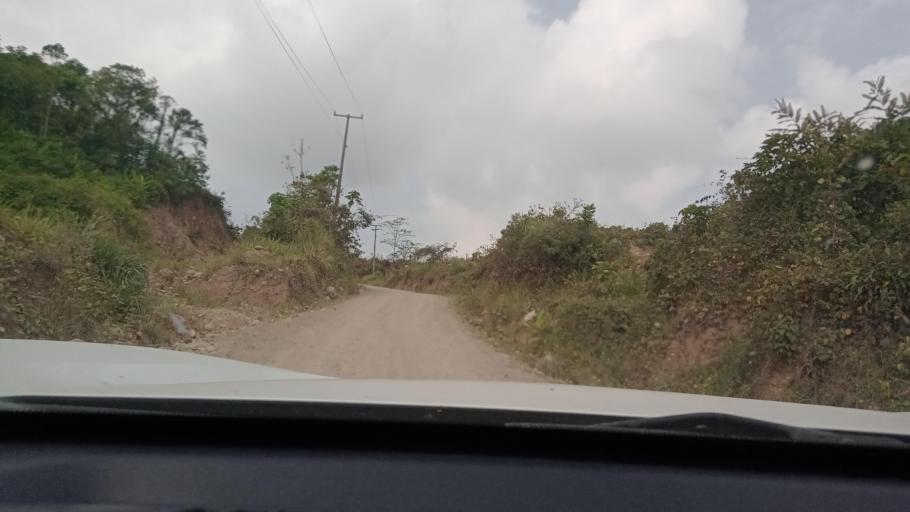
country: MX
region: Tabasco
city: Chontalpa
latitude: 17.4937
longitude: -93.6606
